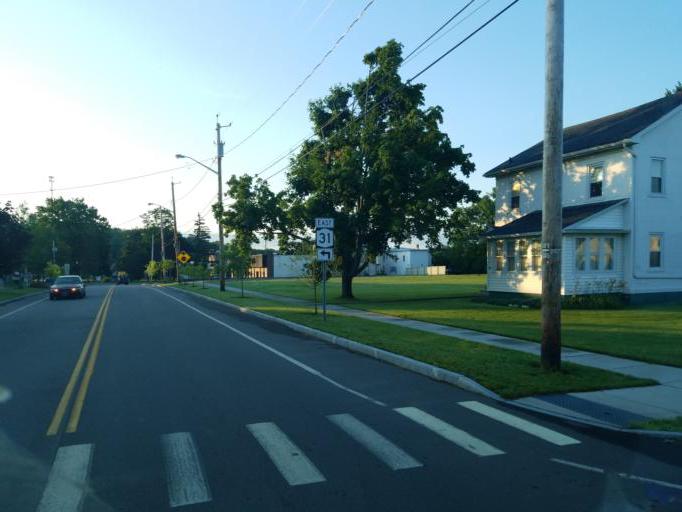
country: US
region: New York
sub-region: Wayne County
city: Clyde
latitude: 43.0849
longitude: -76.8729
